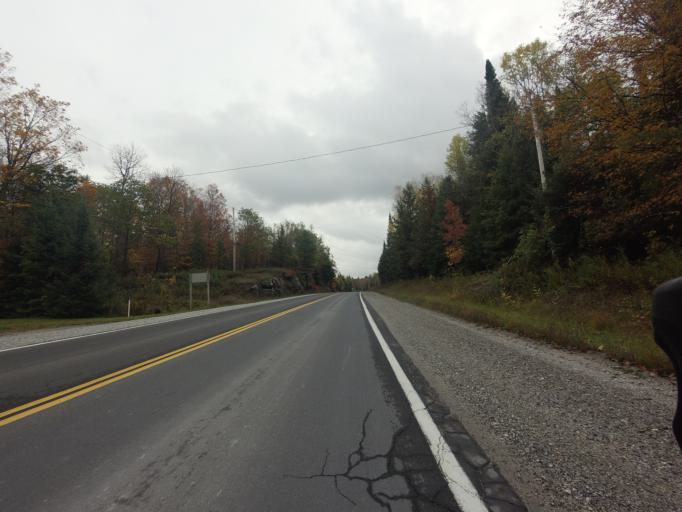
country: CA
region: Ontario
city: Perth
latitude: 45.1186
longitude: -76.4930
